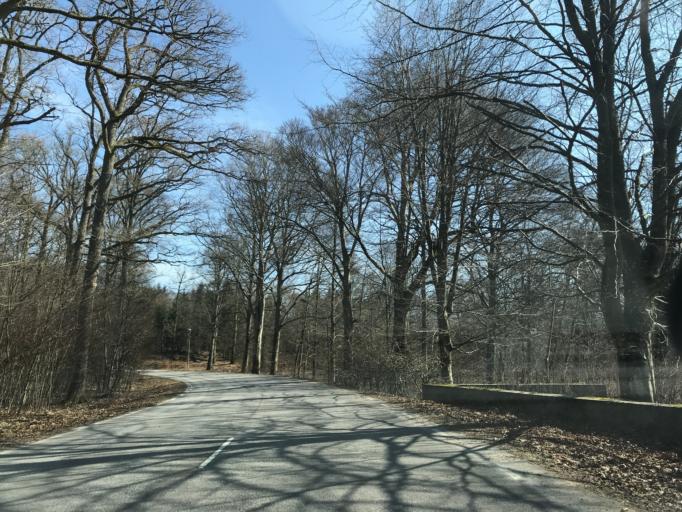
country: SE
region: Skane
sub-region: Hoors Kommun
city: Satofta
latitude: 55.9107
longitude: 13.5297
